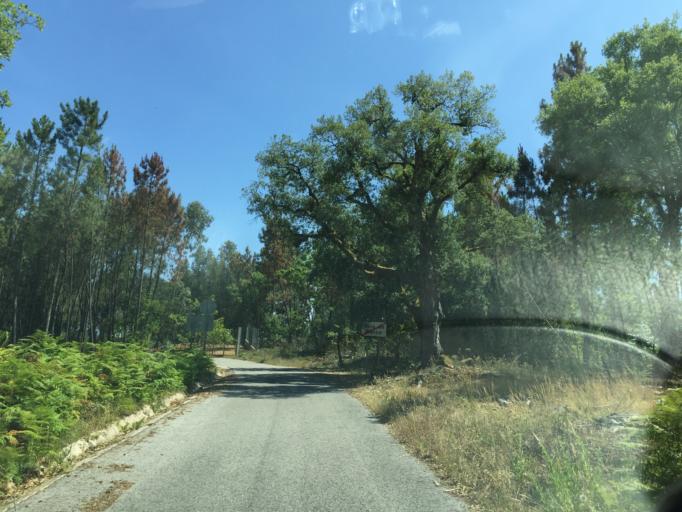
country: PT
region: Leiria
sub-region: Pedrogao Grande
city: Pedrogao Grande
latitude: 39.9282
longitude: -8.1431
